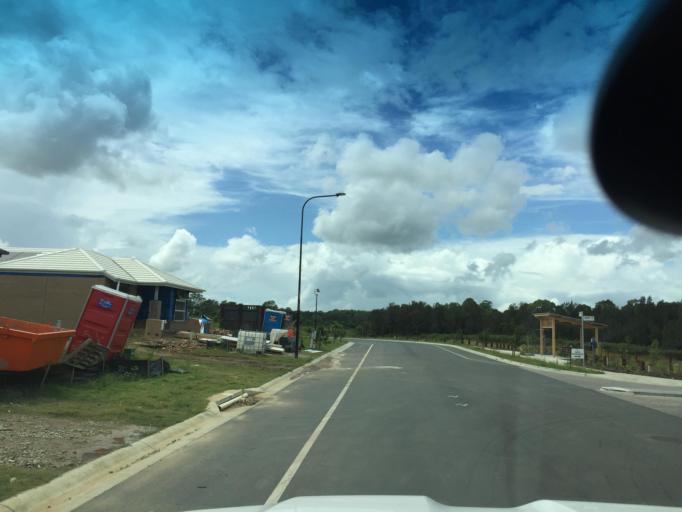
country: AU
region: Queensland
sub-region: Moreton Bay
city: Caboolture South
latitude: -27.0972
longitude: 152.9616
